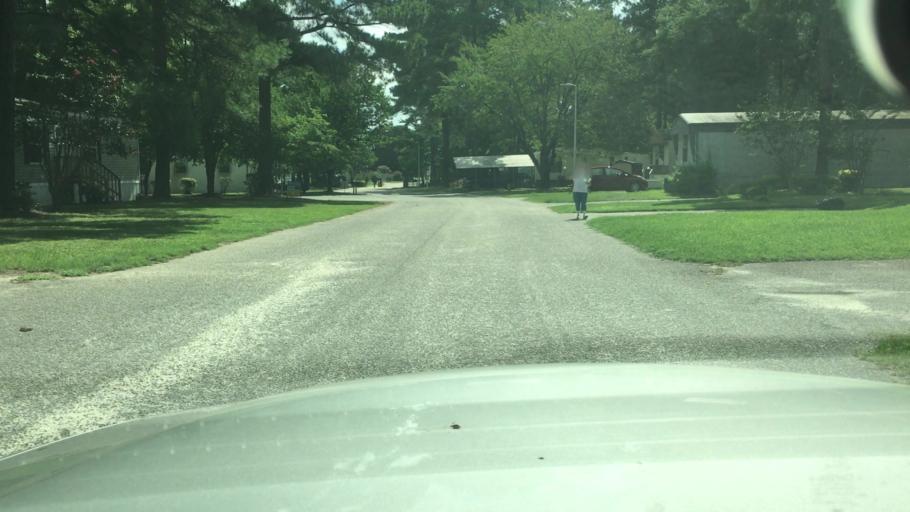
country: US
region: North Carolina
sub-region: Cumberland County
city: Fayetteville
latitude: 35.0052
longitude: -78.9029
